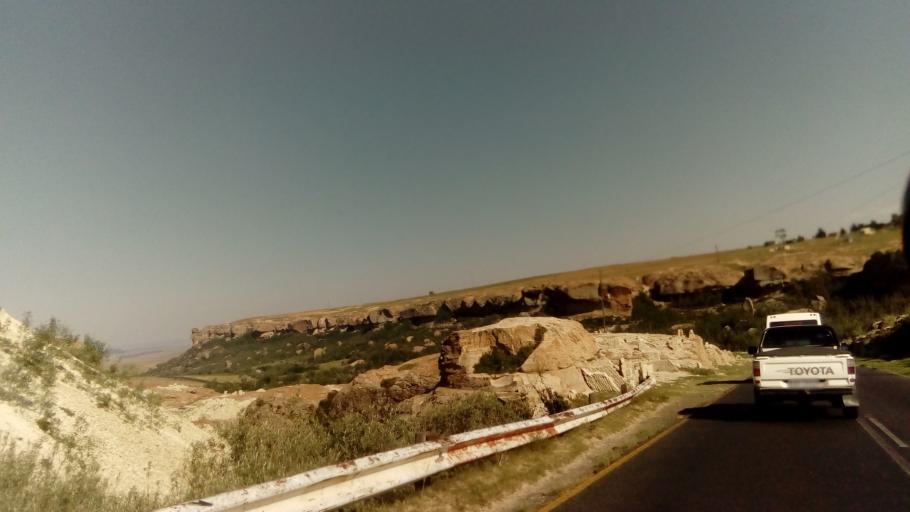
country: LS
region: Berea
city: Teyateyaneng
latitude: -29.1544
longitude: 27.6753
